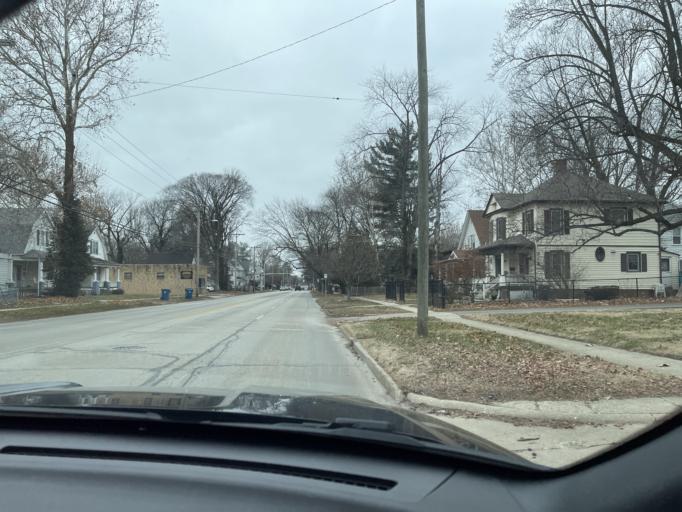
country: US
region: Illinois
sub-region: Sangamon County
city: Springfield
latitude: 39.7943
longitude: -89.6608
